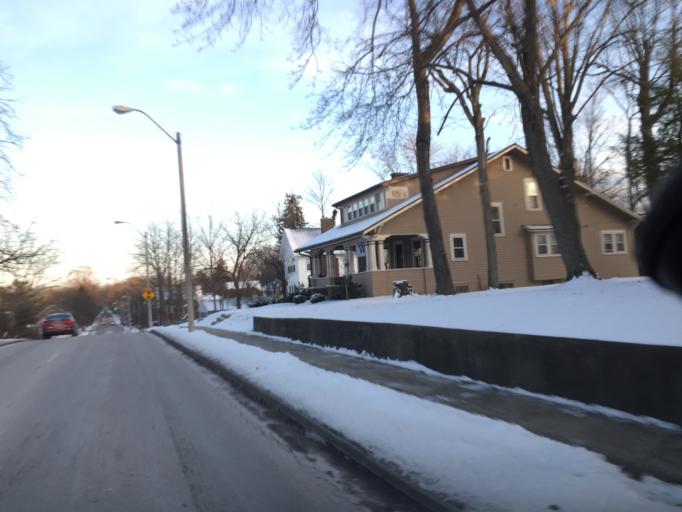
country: US
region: Indiana
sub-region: Monroe County
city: Bloomington
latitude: 39.1631
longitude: -86.5190
